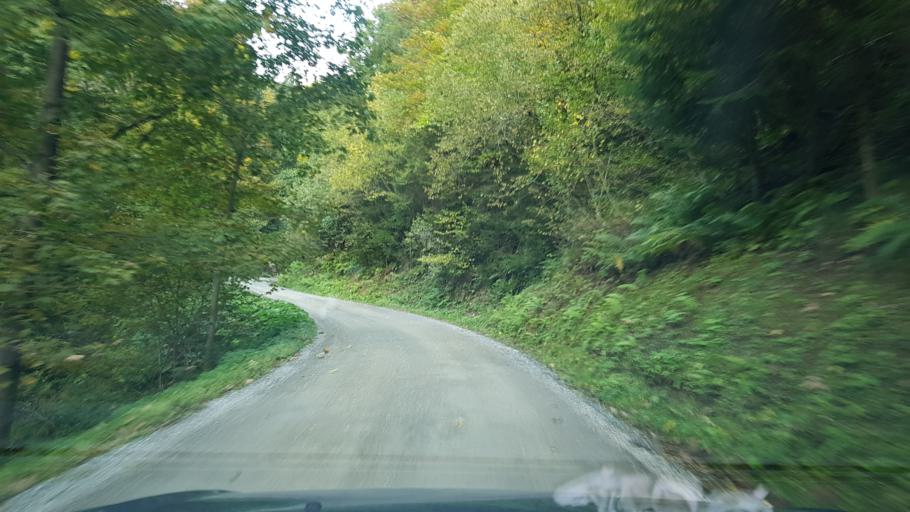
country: SI
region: Slovenj Gradec
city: Legen
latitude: 46.5187
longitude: 15.1306
